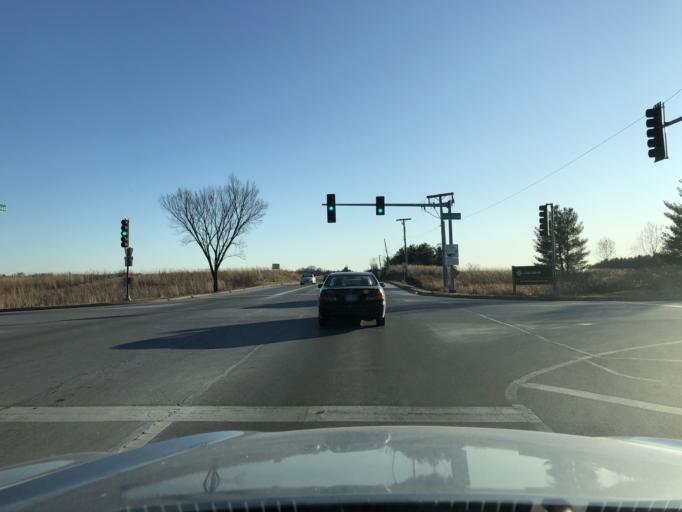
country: US
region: Illinois
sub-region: Lake County
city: Lake Zurich
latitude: 42.1760
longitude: -88.1017
